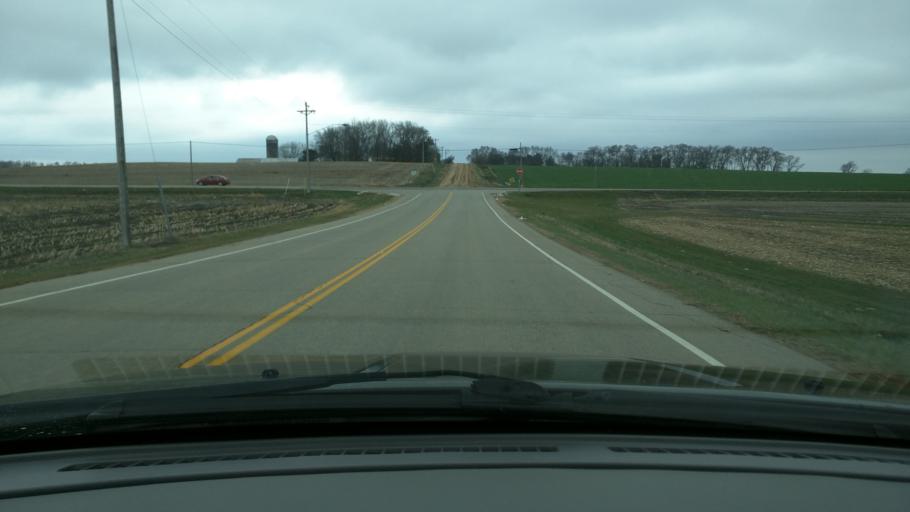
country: US
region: Minnesota
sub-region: Dakota County
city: Hastings
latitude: 44.7576
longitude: -92.9239
